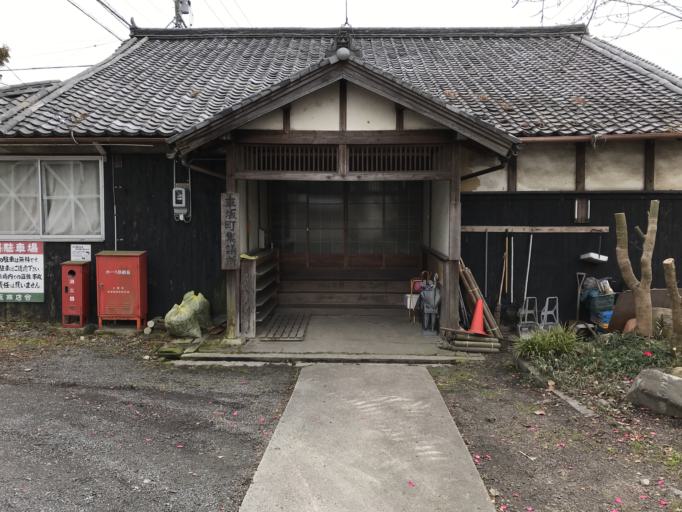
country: JP
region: Mie
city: Ueno-ebisumachi
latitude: 34.7676
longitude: 136.1401
